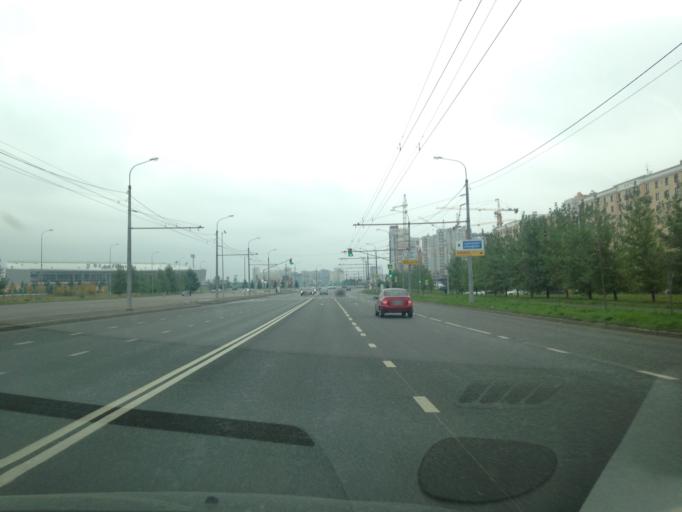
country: RU
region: Tatarstan
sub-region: Gorod Kazan'
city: Kazan
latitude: 55.7887
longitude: 49.1874
